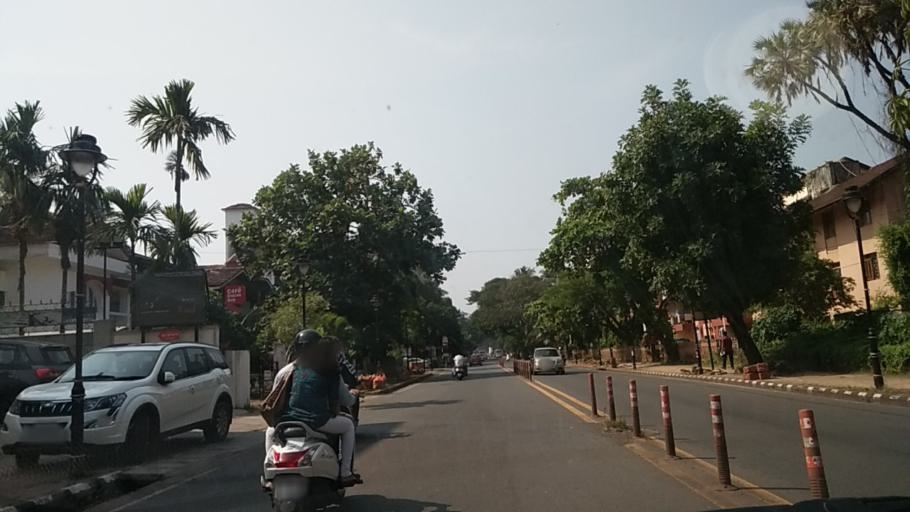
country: IN
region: Goa
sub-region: North Goa
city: Panaji
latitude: 15.4859
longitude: 73.8114
